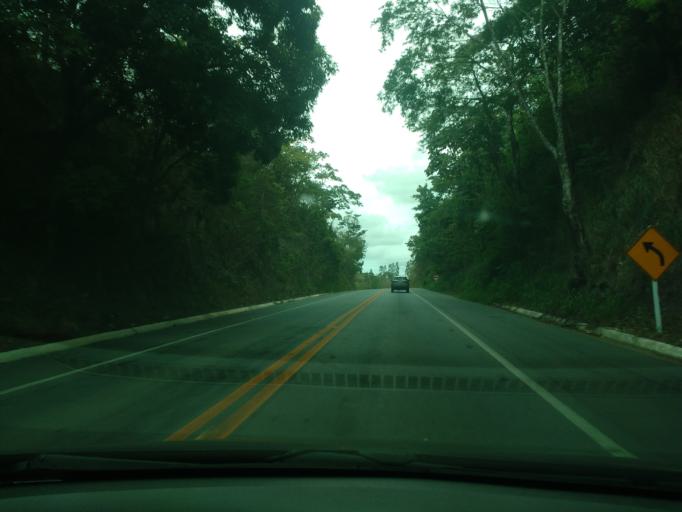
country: BR
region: Alagoas
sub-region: Uniao Dos Palmares
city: Uniao dos Palmares
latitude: -9.2438
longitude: -36.0098
